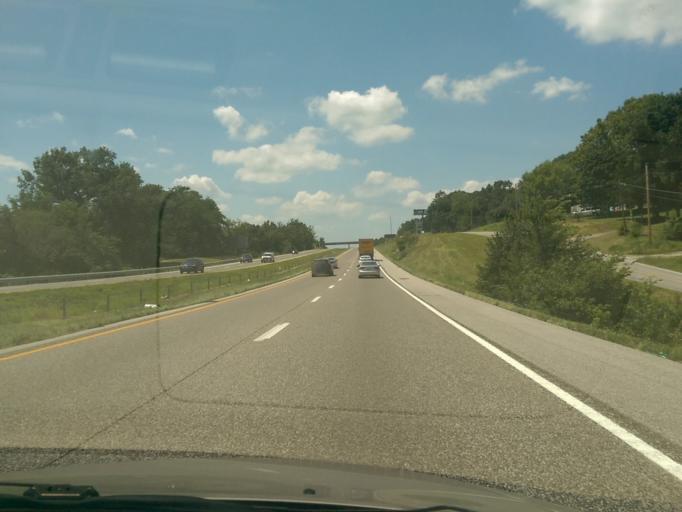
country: US
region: Missouri
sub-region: Boone County
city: Columbia
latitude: 38.9706
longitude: -92.3956
